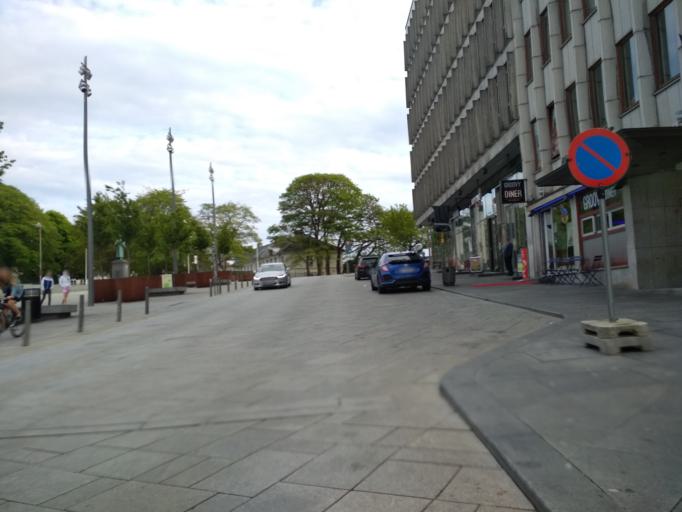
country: NO
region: Rogaland
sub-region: Stavanger
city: Stavanger
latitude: 58.9702
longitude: 5.7310
